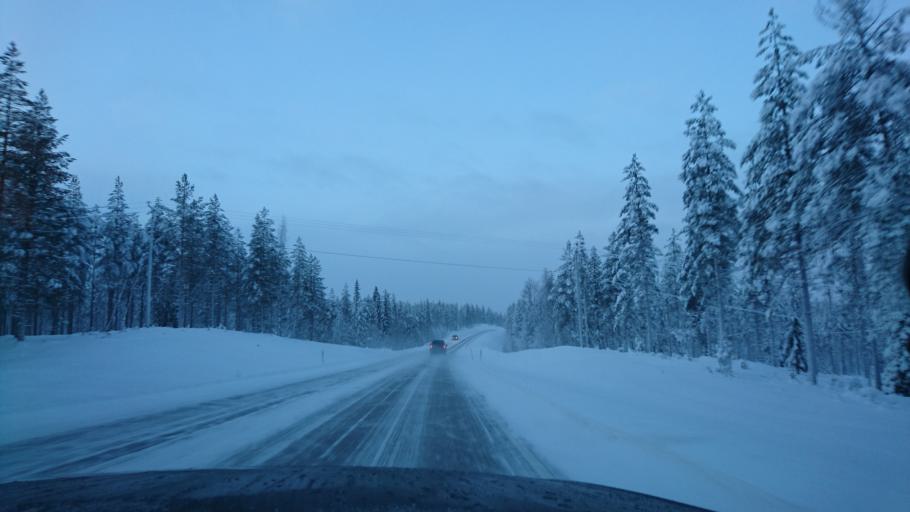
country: FI
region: Northern Ostrobothnia
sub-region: Koillismaa
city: Taivalkoski
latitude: 65.4681
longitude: 27.7144
